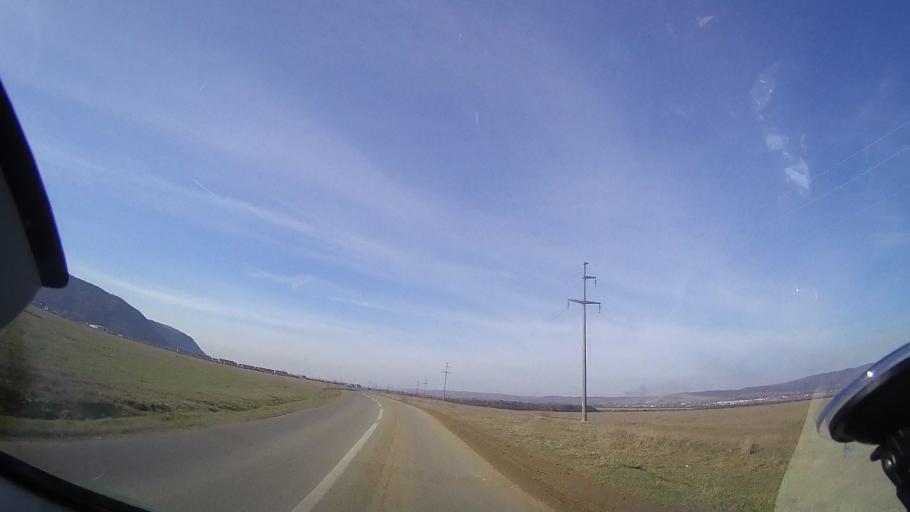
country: RO
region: Bihor
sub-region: Comuna Magesti
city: Magesti
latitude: 47.0214
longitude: 22.4179
